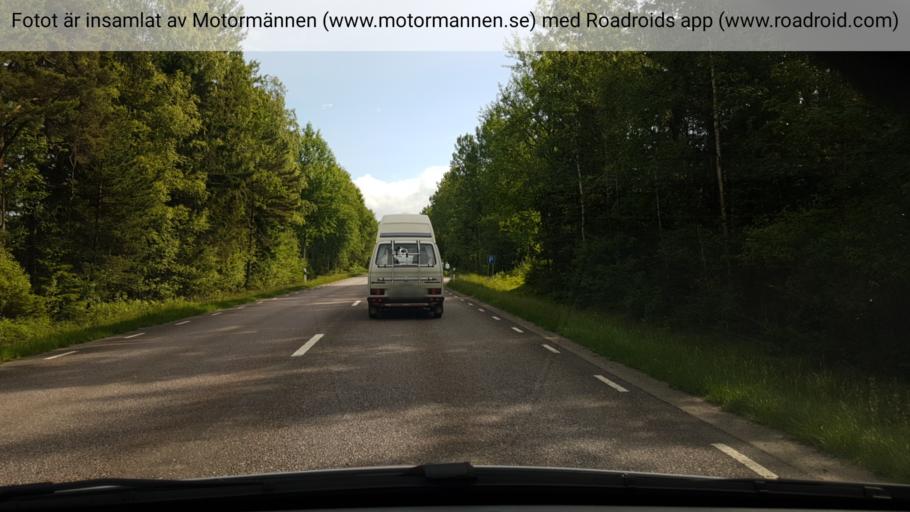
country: SE
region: Vaestra Goetaland
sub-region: Karlsborgs Kommun
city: Molltorp
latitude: 58.4953
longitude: 14.4523
